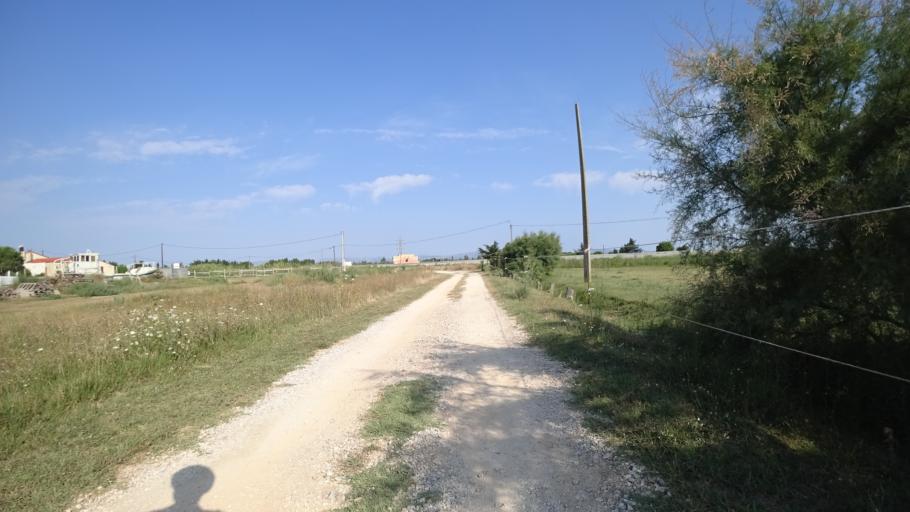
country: FR
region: Languedoc-Roussillon
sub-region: Departement des Pyrenees-Orientales
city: Saint-Laurent-de-la-Salanque
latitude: 42.7867
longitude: 3.0058
